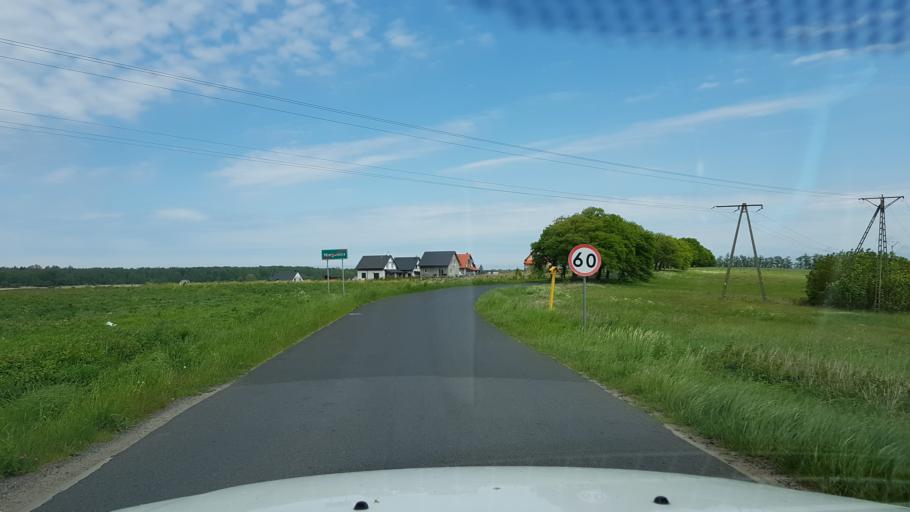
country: PL
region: West Pomeranian Voivodeship
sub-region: Powiat koszalinski
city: Mielno
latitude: 54.2422
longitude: 15.9930
